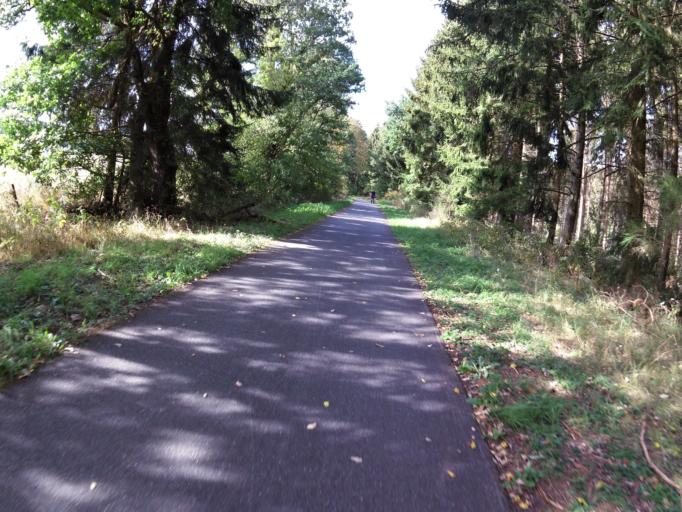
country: DE
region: Rheinland-Pfalz
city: Bleialf
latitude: 50.2145
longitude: 6.2773
